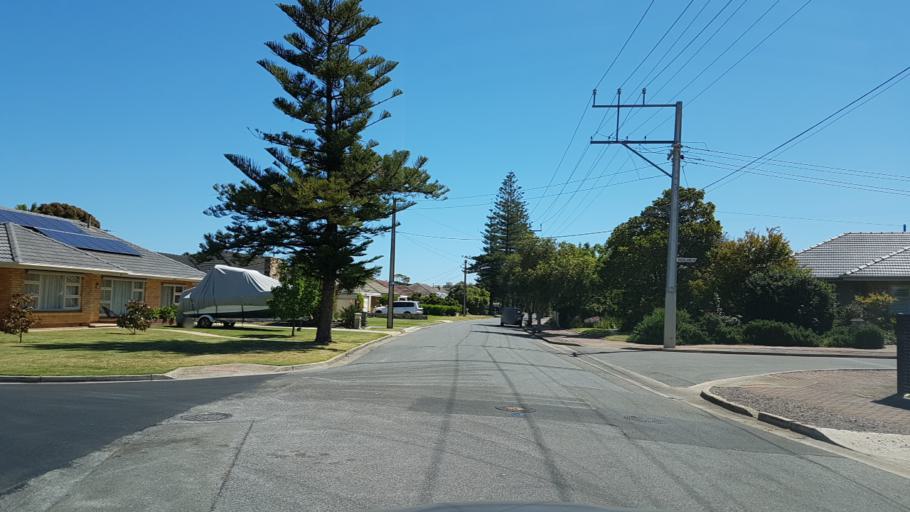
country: AU
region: South Australia
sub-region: Holdfast Bay
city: Glenelg East
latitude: -34.9745
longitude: 138.5279
